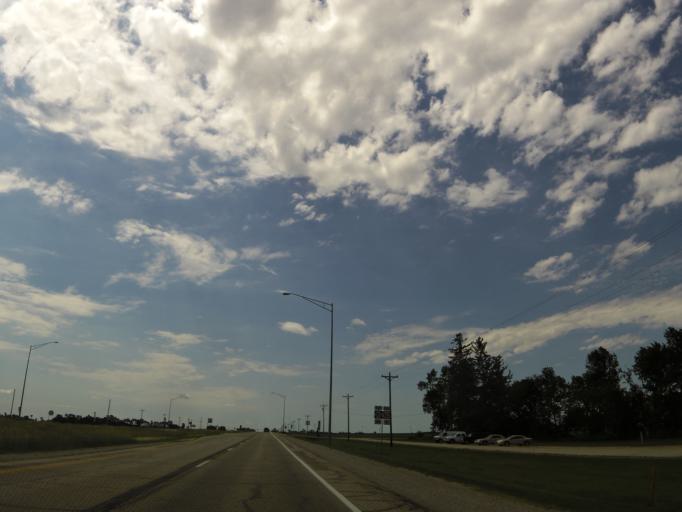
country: US
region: Iowa
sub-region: Bremer County
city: Tripoli
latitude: 42.8043
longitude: -92.3374
